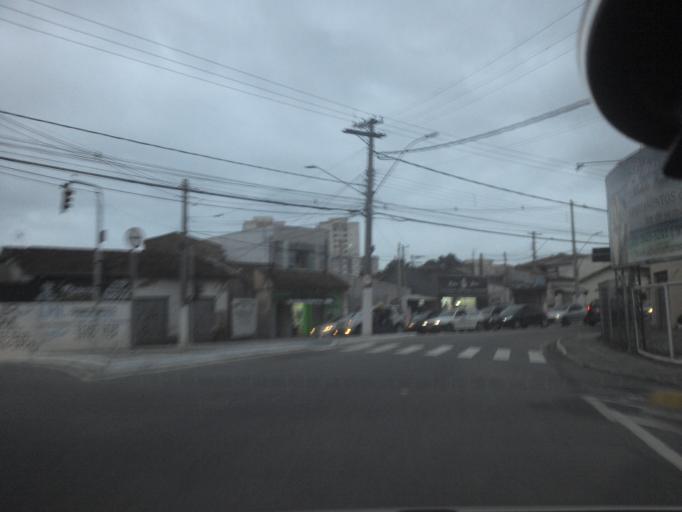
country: BR
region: Sao Paulo
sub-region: Taubate
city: Taubate
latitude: -23.0227
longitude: -45.5485
